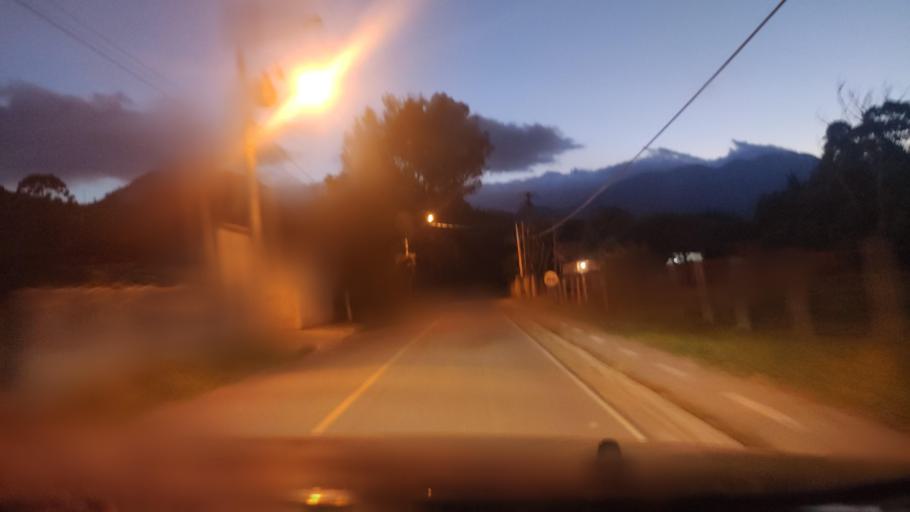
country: BR
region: Minas Gerais
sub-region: Paraisopolis
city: Paraisopolis
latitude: -22.7011
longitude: -45.7539
